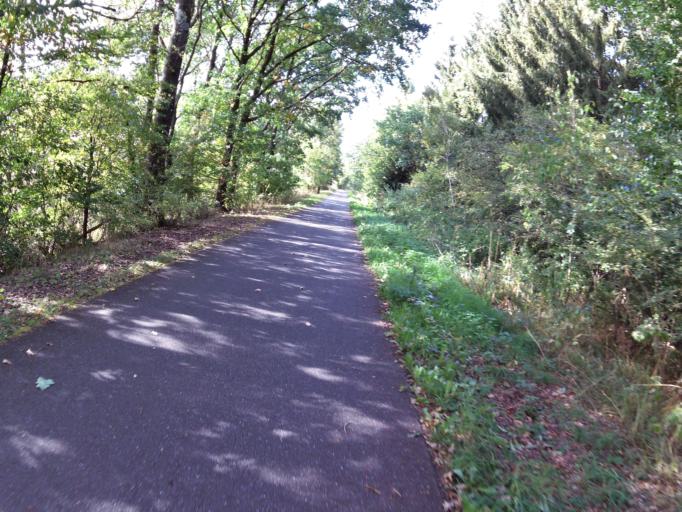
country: DE
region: Rheinland-Pfalz
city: Bleialf
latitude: 50.2166
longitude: 6.2744
